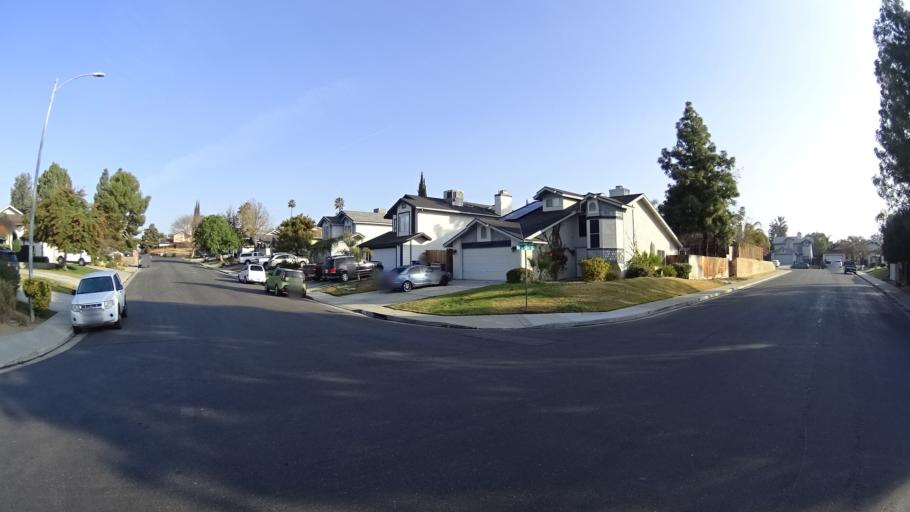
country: US
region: California
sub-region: Kern County
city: Oildale
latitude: 35.3993
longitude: -118.9430
